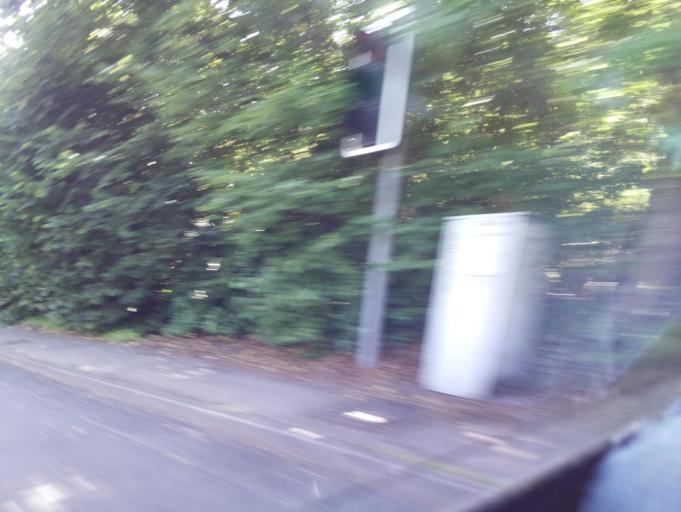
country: GB
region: Wales
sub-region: Caerphilly County Borough
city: Maesycwmmer
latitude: 51.6259
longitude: -3.2321
